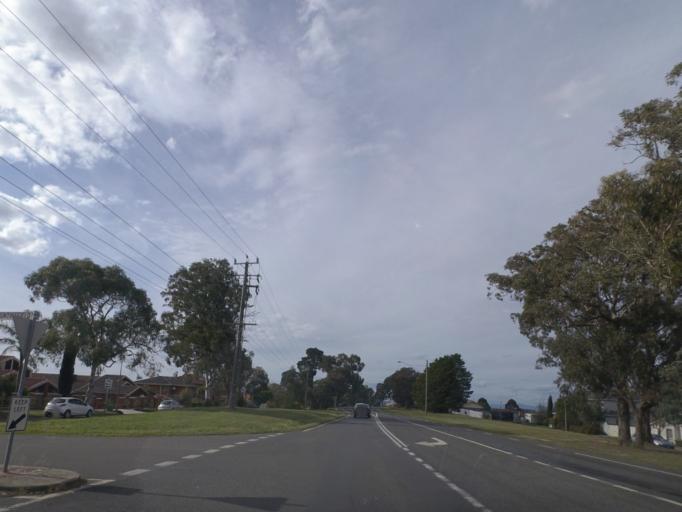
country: AU
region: Victoria
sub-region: Manningham
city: Donvale
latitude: -37.7742
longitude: 145.1686
